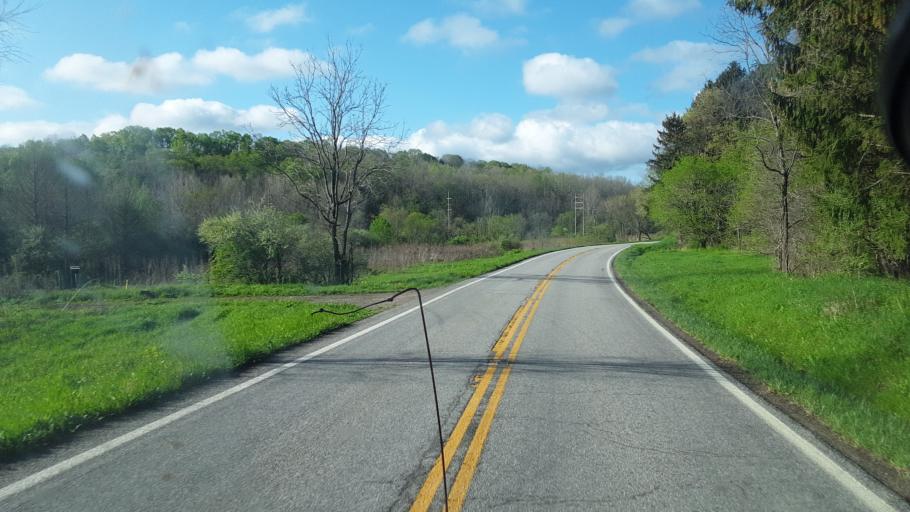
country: US
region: Ohio
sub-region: Noble County
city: Caldwell
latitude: 39.8346
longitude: -81.6639
